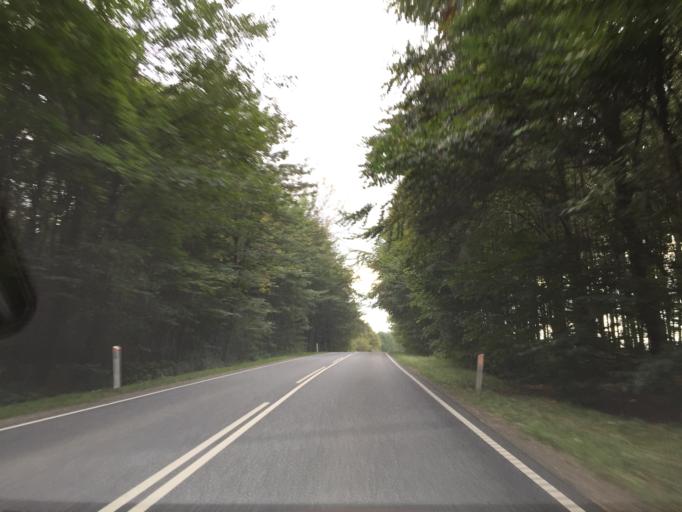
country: DK
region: Central Jutland
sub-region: Favrskov Kommune
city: Ulstrup
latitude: 56.3280
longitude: 9.8212
